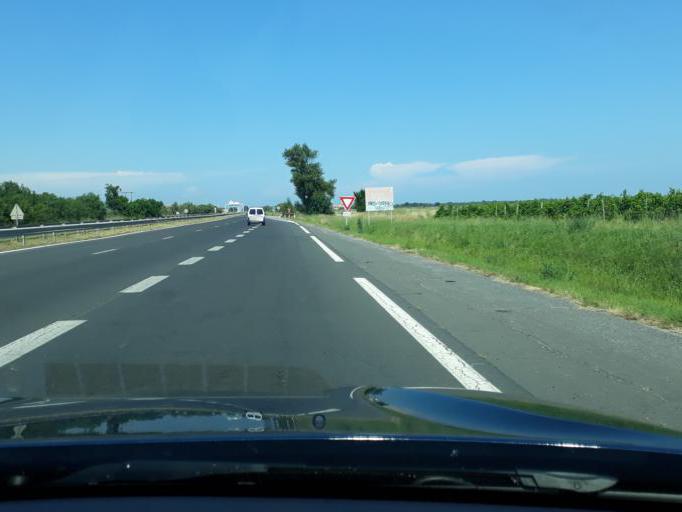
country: FR
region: Languedoc-Roussillon
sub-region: Departement de l'Herault
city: Le Cap d'Agde
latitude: 43.3083
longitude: 3.5114
